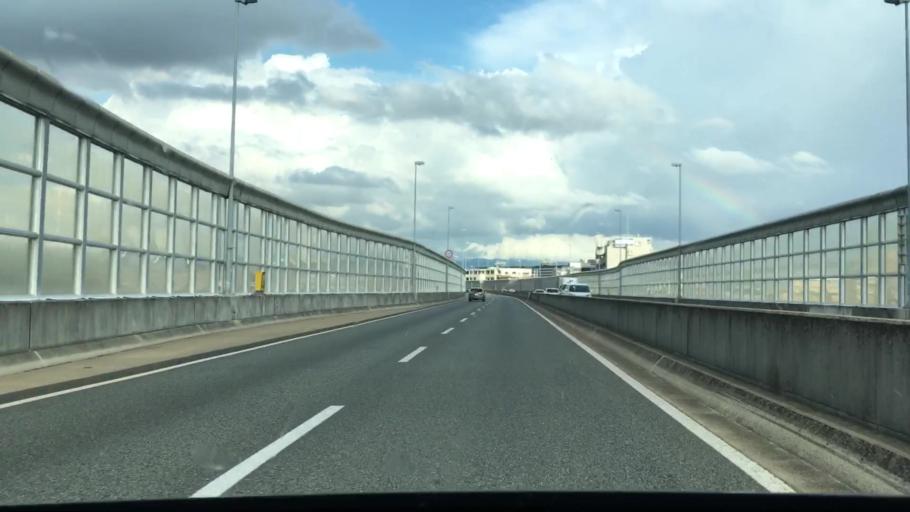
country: JP
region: Fukuoka
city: Fukuoka-shi
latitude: 33.5782
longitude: 130.3220
